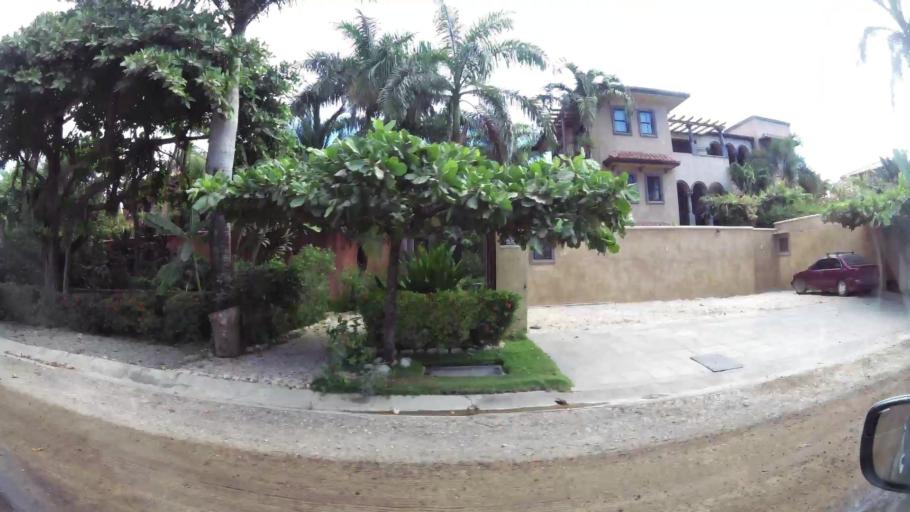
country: CR
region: Guanacaste
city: Santa Cruz
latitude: 10.2887
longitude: -85.8511
